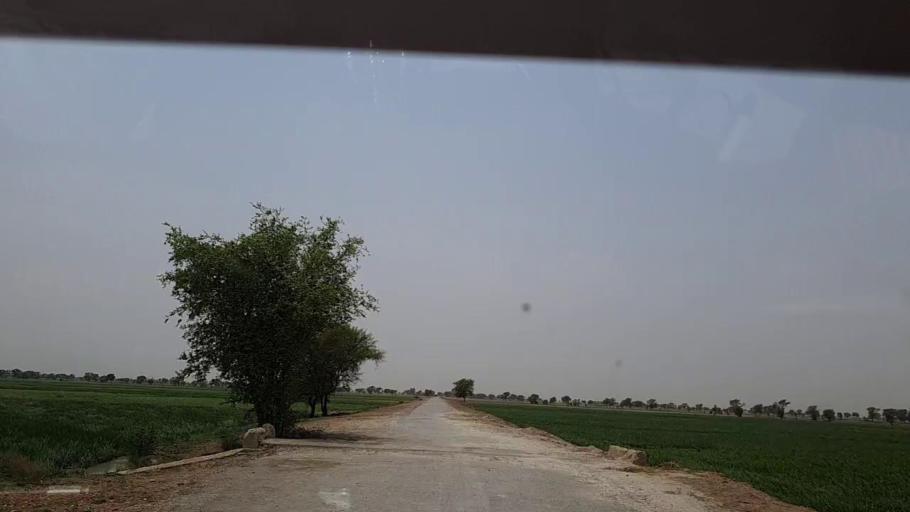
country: PK
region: Sindh
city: Khairpur Nathan Shah
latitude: 27.0060
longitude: 67.6432
